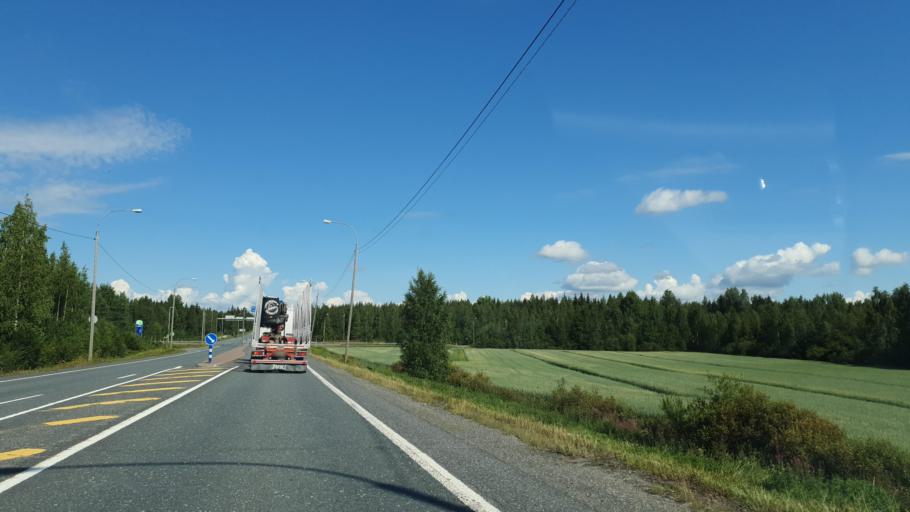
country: FI
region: Northern Savo
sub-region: Ylae-Savo
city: Iisalmi
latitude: 63.6249
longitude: 27.2251
